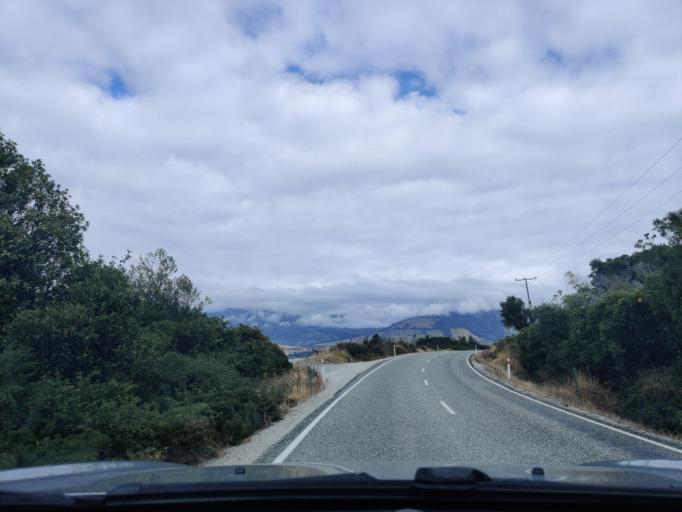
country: NZ
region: Otago
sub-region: Queenstown-Lakes District
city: Queenstown
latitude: -45.0804
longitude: 168.4728
